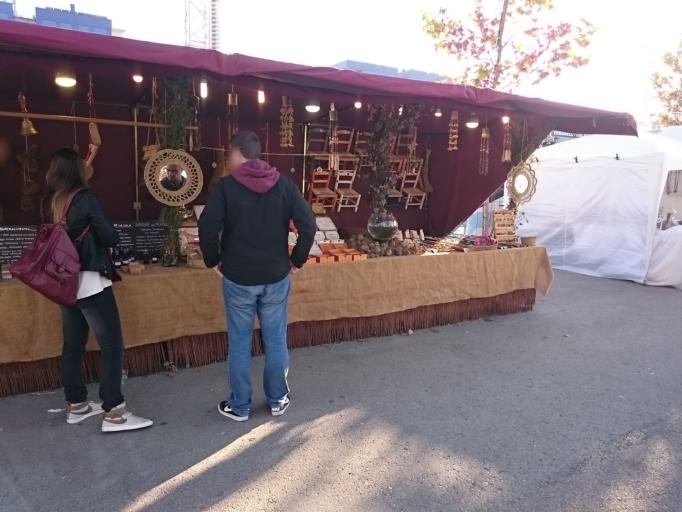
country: ES
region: Catalonia
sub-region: Provincia de Barcelona
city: Vilanova i la Geltru
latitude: 41.2178
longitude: 1.7272
